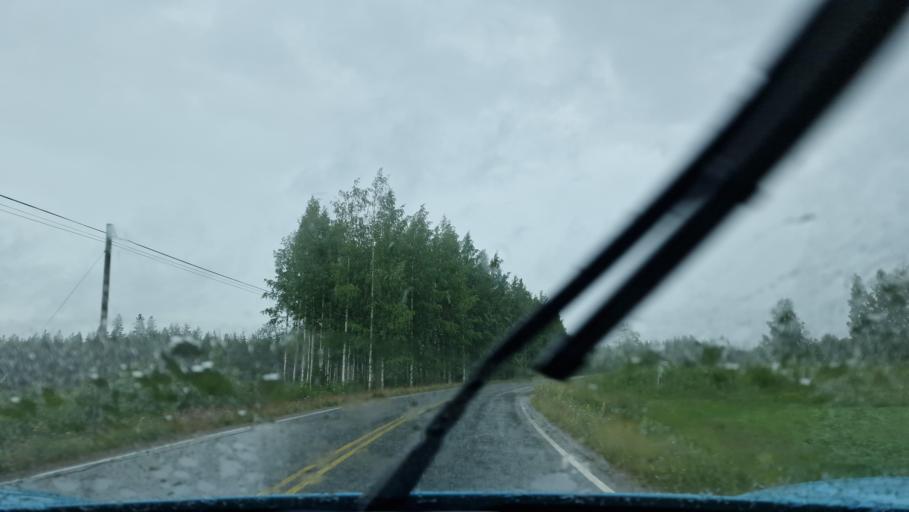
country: FI
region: Southern Ostrobothnia
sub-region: Jaerviseutu
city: Soini
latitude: 62.8292
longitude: 24.3397
